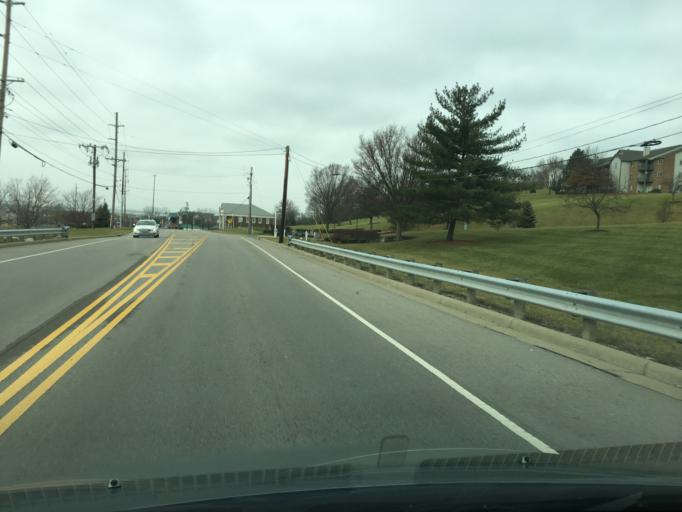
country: US
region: Ohio
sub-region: Butler County
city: Beckett Ridge
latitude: 39.3272
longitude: -84.4195
